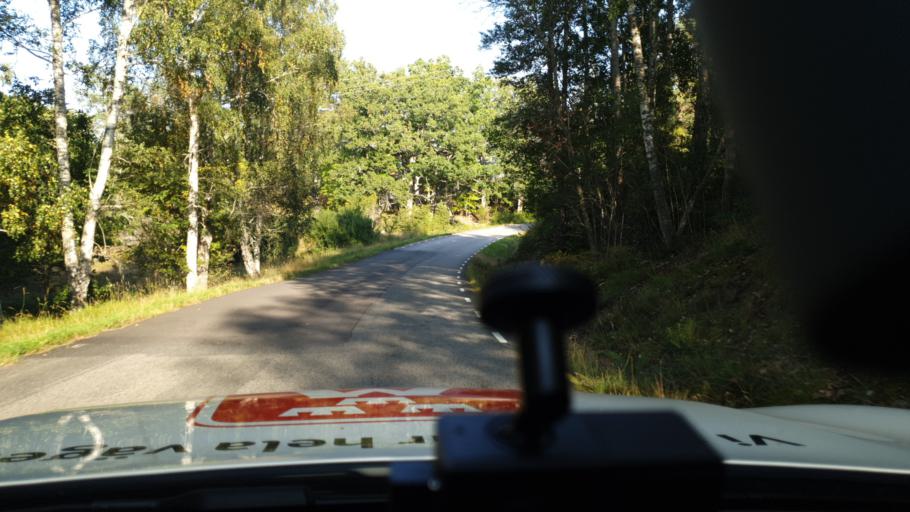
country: SE
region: Kalmar
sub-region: Oskarshamns Kommun
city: Oskarshamn
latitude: 57.4387
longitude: 16.4952
